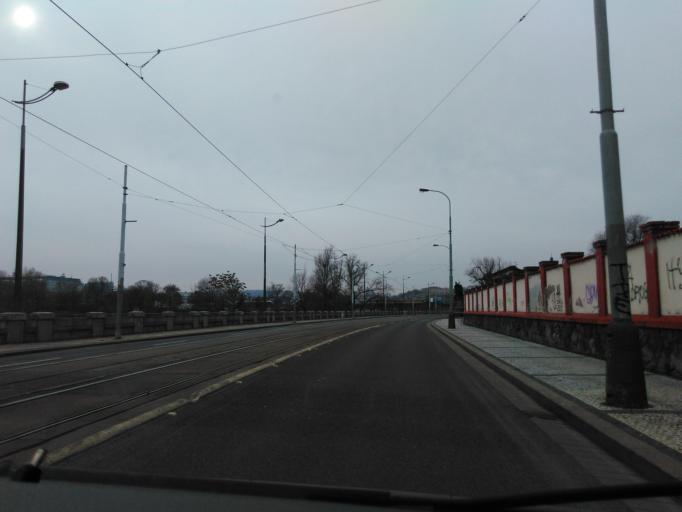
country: CZ
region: Praha
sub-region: Praha 8
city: Karlin
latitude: 50.0984
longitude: 14.4476
